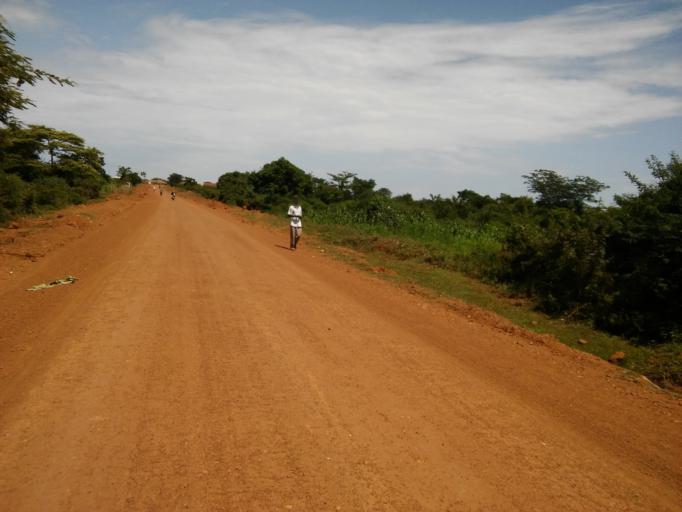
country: UG
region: Eastern Region
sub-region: Kumi District
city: Kumi
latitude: 1.4739
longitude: 33.8742
